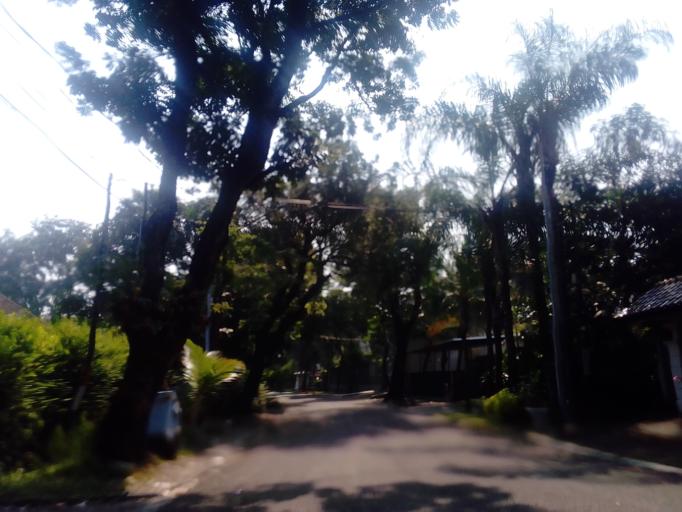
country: ID
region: Jakarta Raya
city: Jakarta
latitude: -6.2513
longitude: 106.8024
